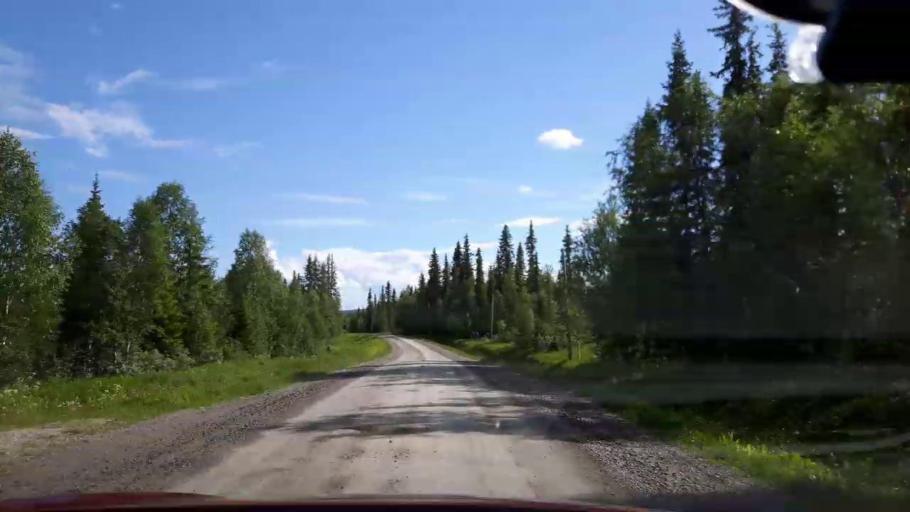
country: SE
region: Jaemtland
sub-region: Krokoms Kommun
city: Valla
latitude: 63.7932
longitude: 14.0467
